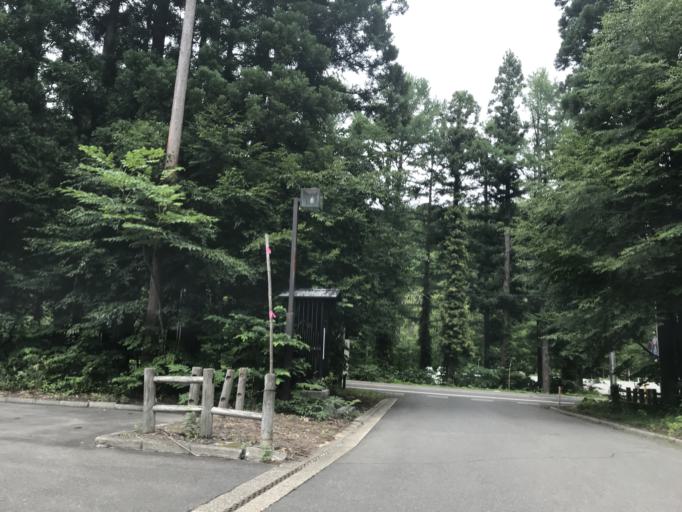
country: JP
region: Iwate
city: Ichinoseki
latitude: 39.0041
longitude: 140.8551
